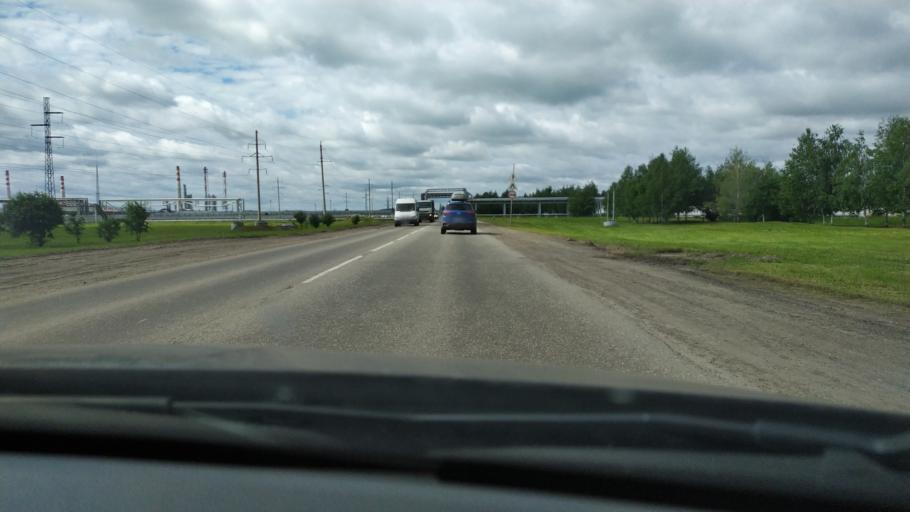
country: RU
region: Perm
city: Kondratovo
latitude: 57.9308
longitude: 56.1232
